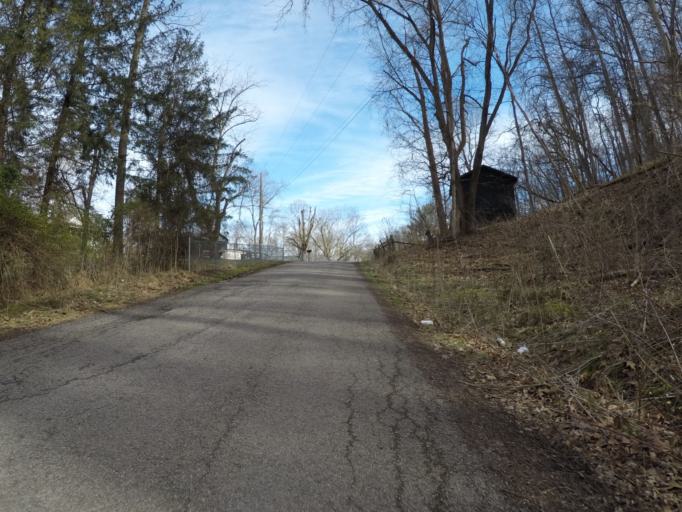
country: US
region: West Virginia
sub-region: Wayne County
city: Lavalette
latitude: 38.3420
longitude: -82.5076
